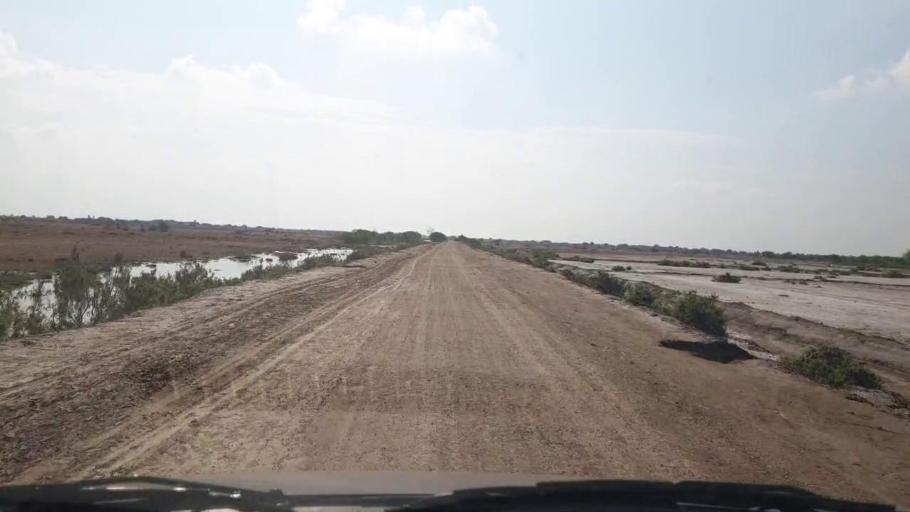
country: PK
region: Sindh
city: Badin
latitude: 24.4960
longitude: 68.6119
